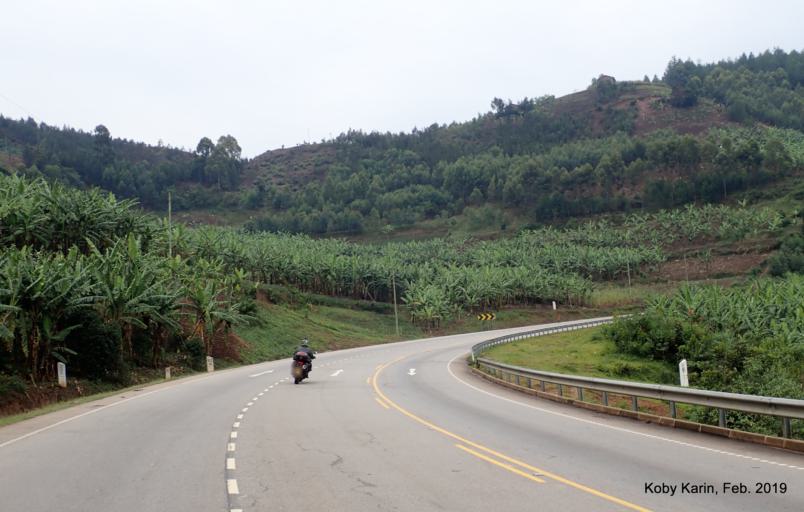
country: UG
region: Western Region
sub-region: Kabale District
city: Kabale
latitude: -1.2346
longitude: 30.0579
